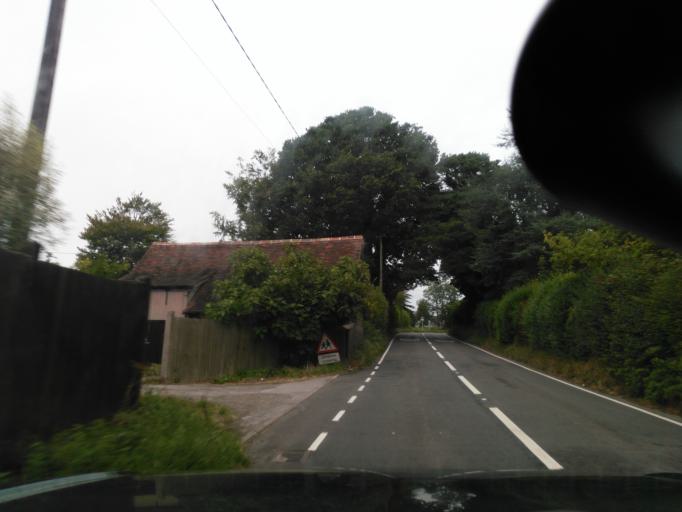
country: GB
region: England
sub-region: Dorset
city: Shaftesbury
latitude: 50.9426
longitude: -2.1942
